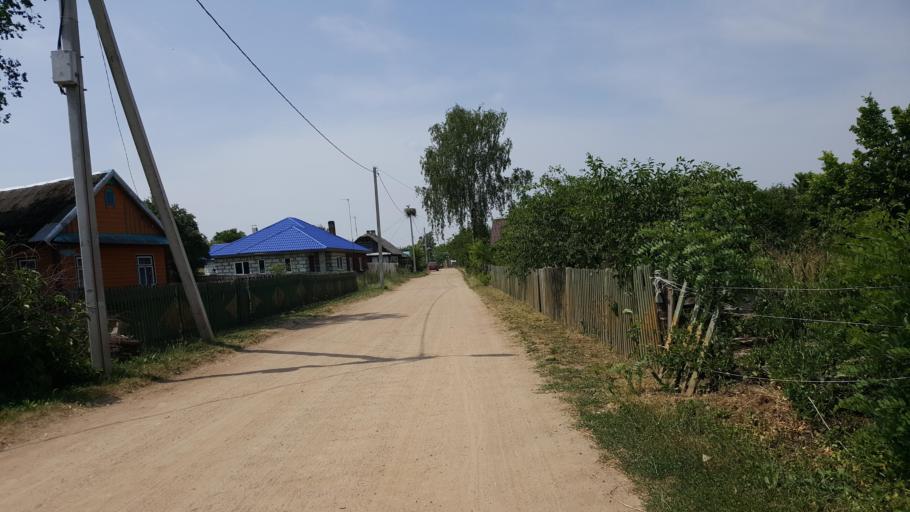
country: BY
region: Brest
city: Kamyanyets
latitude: 52.3731
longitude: 23.7821
